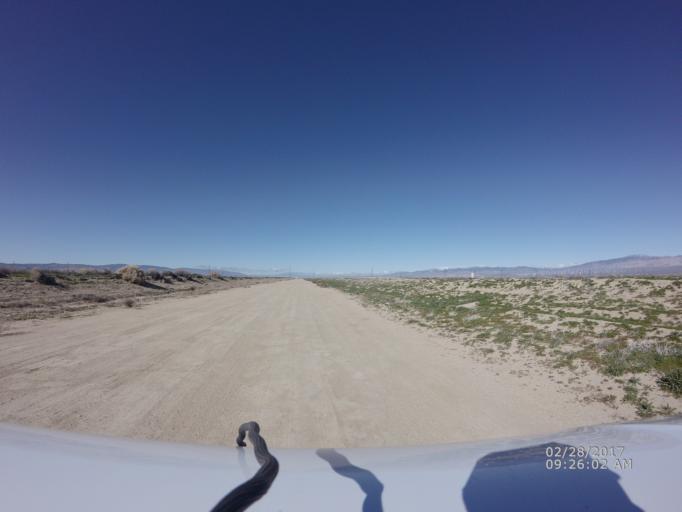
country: US
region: California
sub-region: Kern County
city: Rosamond
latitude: 34.8051
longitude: -118.3292
